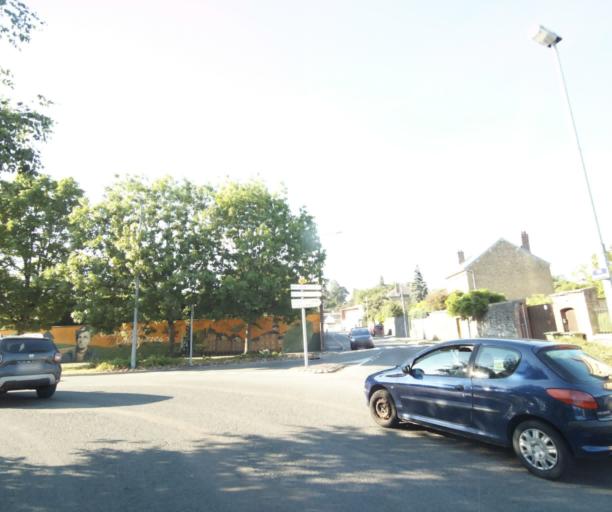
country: FR
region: Champagne-Ardenne
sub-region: Departement des Ardennes
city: Charleville-Mezieres
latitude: 49.7809
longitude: 4.7155
